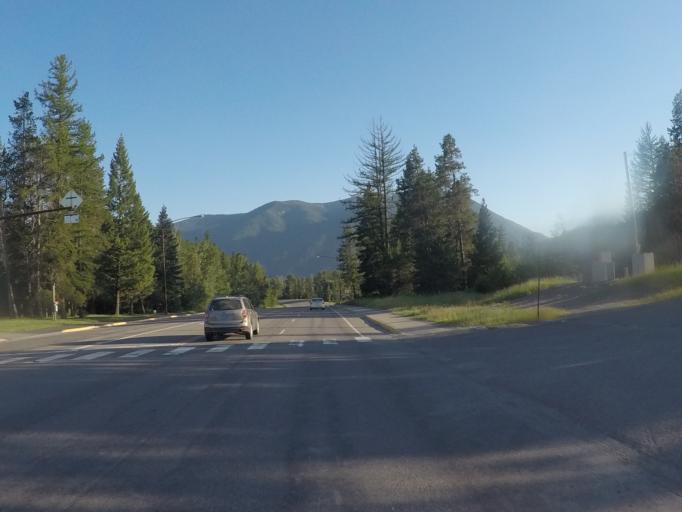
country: US
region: Montana
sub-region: Flathead County
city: Columbia Falls
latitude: 48.4179
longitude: -114.0473
